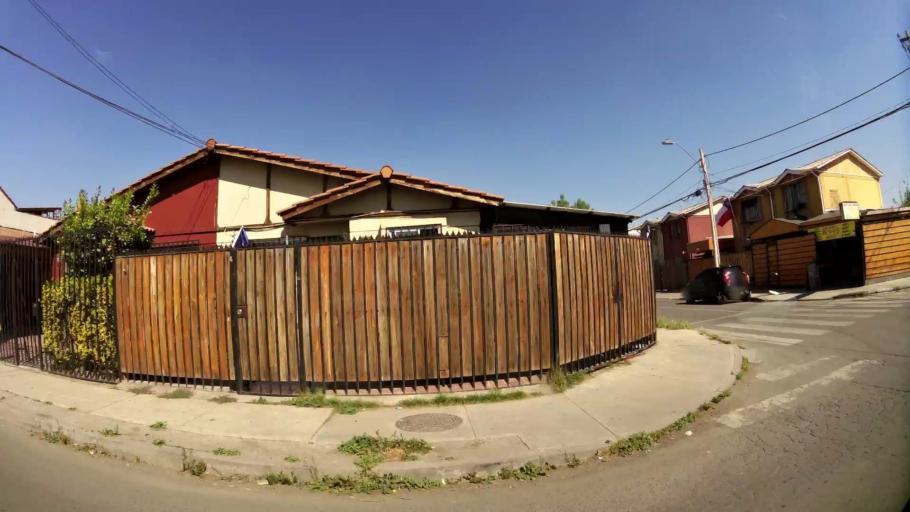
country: CL
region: Santiago Metropolitan
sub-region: Provincia de Santiago
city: Lo Prado
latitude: -33.3495
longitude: -70.7441
